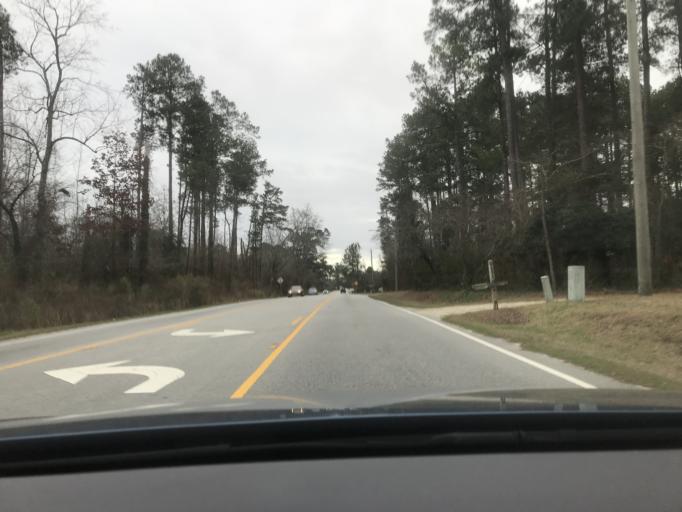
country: US
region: North Carolina
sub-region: Hoke County
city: Rockfish
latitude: 35.0489
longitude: -79.0103
